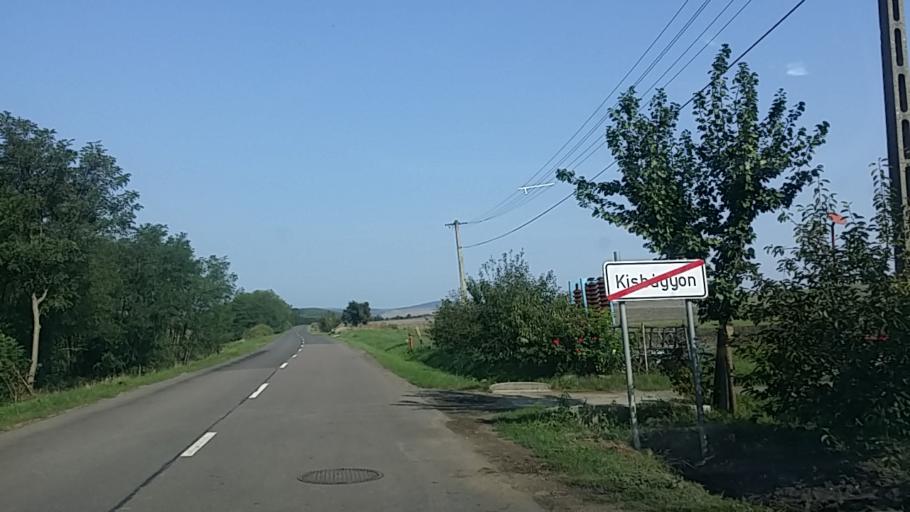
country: HU
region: Nograd
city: Palotas
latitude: 47.8274
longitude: 19.5871
